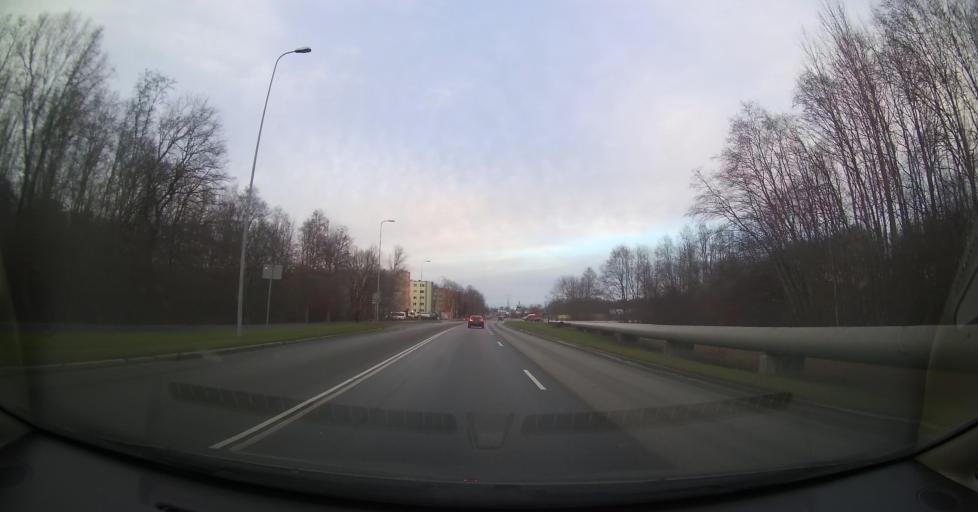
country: EE
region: Ida-Virumaa
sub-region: Johvi vald
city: Johvi
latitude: 59.3450
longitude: 27.4193
